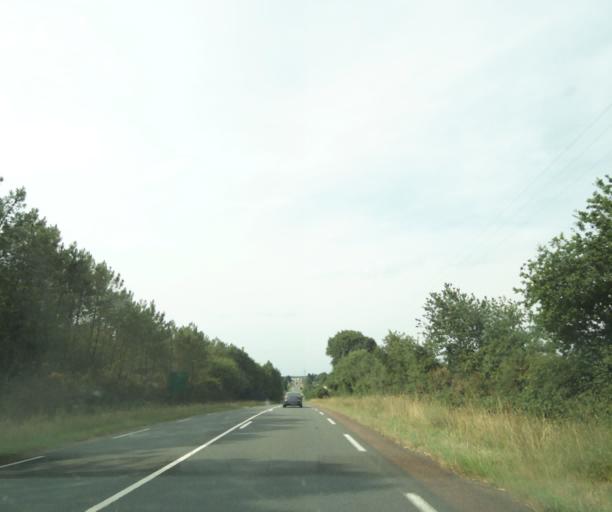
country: FR
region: Pays de la Loire
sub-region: Departement de la Sarthe
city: Marigne-Laille
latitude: 47.7837
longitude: 0.3395
